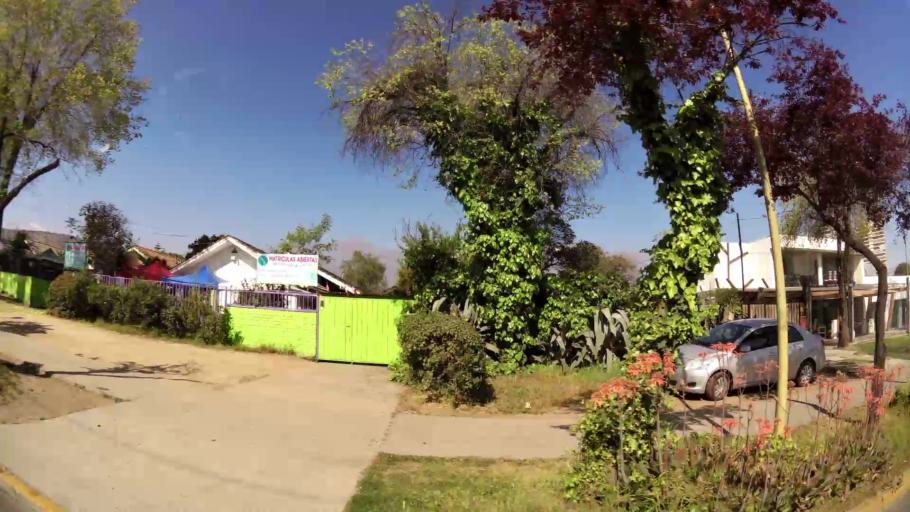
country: CL
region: Santiago Metropolitan
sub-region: Provincia de Santiago
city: Villa Presidente Frei, Nunoa, Santiago, Chile
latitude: -33.4043
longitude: -70.5497
